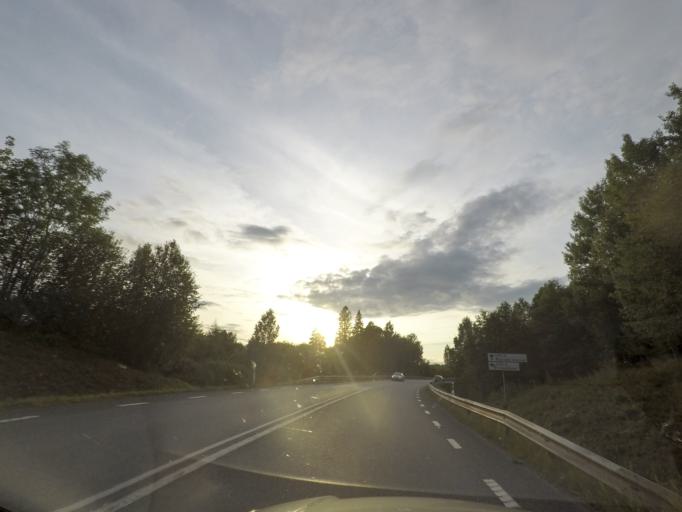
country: SE
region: OErebro
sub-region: Nora Kommun
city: As
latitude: 59.5072
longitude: 14.9683
